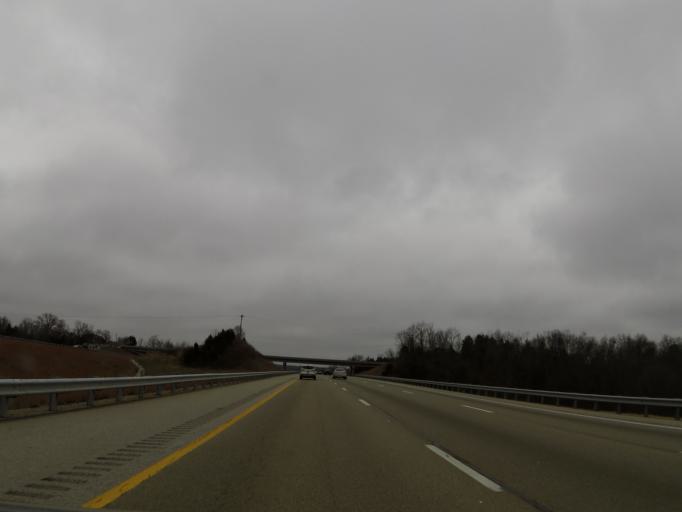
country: US
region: Kentucky
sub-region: Grant County
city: Williamstown
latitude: 38.5574
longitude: -84.5975
